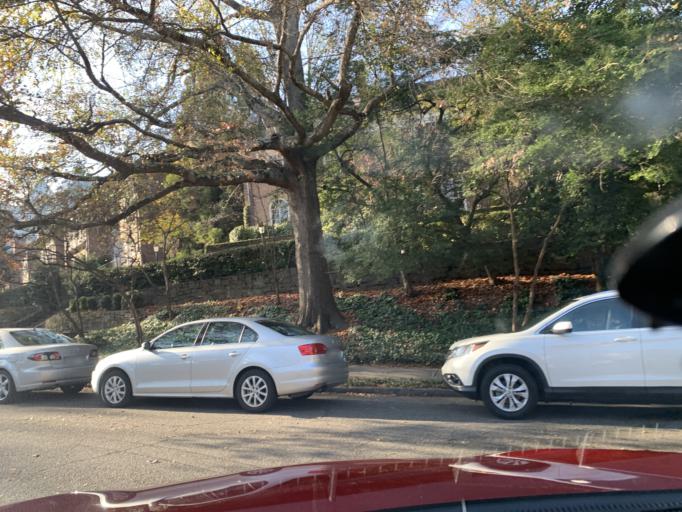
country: US
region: Georgia
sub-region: Fulton County
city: Atlanta
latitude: 33.7889
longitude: -84.3786
